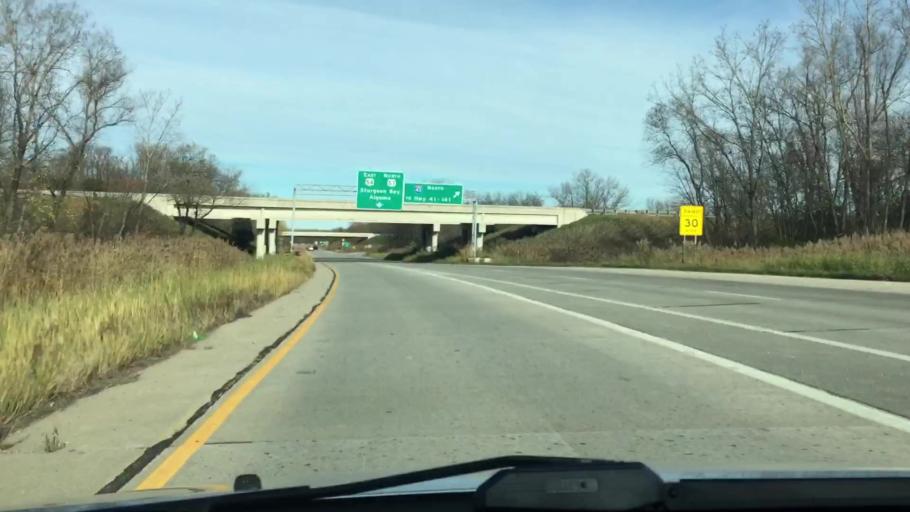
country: US
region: Wisconsin
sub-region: Brown County
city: Green Bay
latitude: 44.5176
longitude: -87.9545
